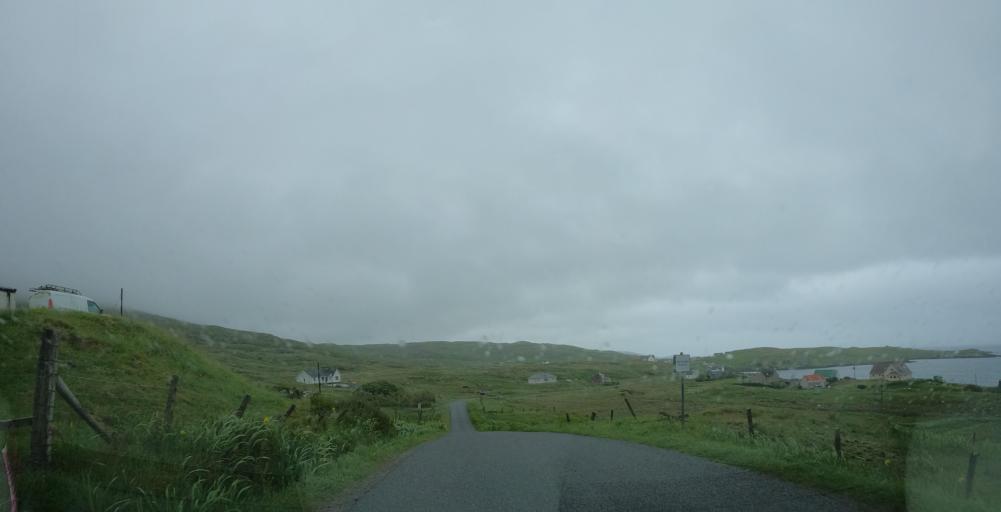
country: GB
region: Scotland
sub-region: Eilean Siar
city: Barra
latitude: 56.9621
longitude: -7.4458
